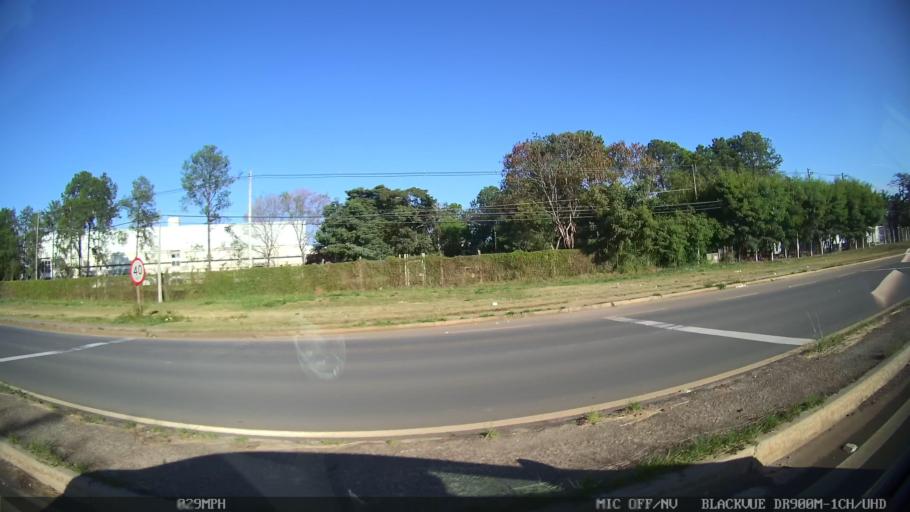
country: BR
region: Sao Paulo
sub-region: Nova Odessa
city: Nova Odessa
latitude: -22.7636
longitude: -47.2562
